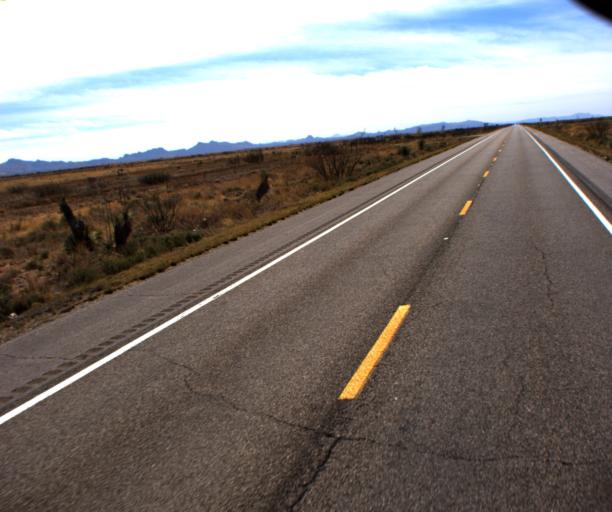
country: US
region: Arizona
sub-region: Cochise County
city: Pirtleville
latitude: 31.5266
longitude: -109.6493
